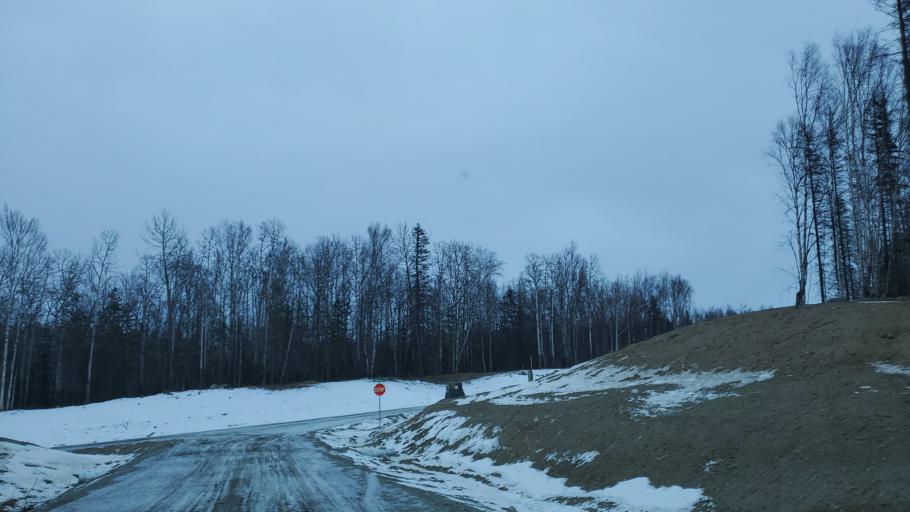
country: US
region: Alaska
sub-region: Matanuska-Susitna Borough
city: Gateway
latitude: 61.6566
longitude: -149.2323
